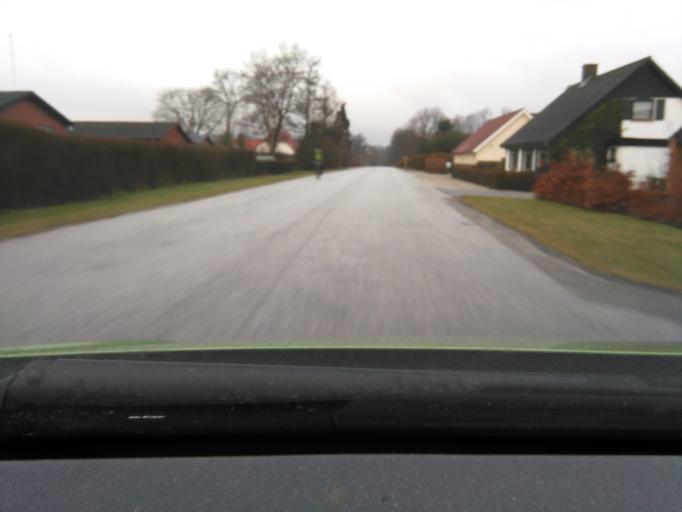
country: DK
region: Central Jutland
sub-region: Arhus Kommune
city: Beder
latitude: 56.0614
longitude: 10.2054
